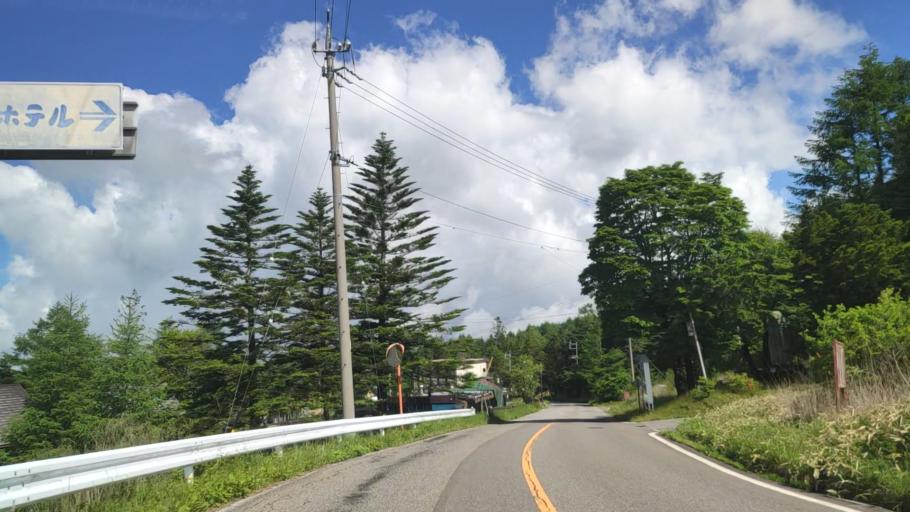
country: JP
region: Nagano
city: Suwa
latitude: 36.0973
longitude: 138.1636
